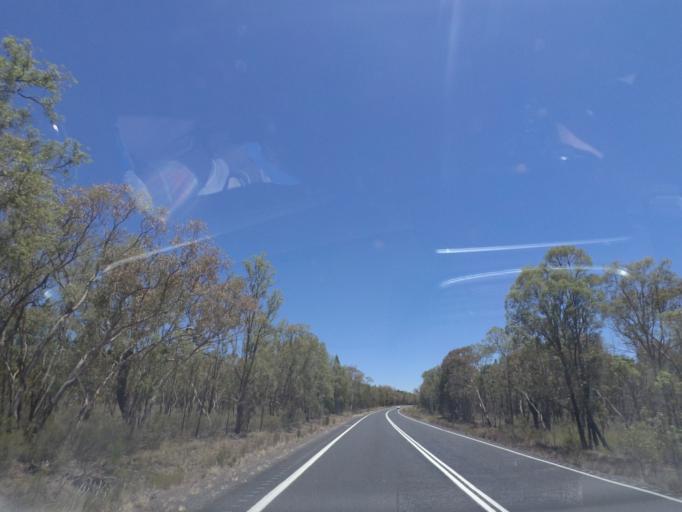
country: AU
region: New South Wales
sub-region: Warrumbungle Shire
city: Coonabarabran
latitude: -31.1957
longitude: 149.3508
